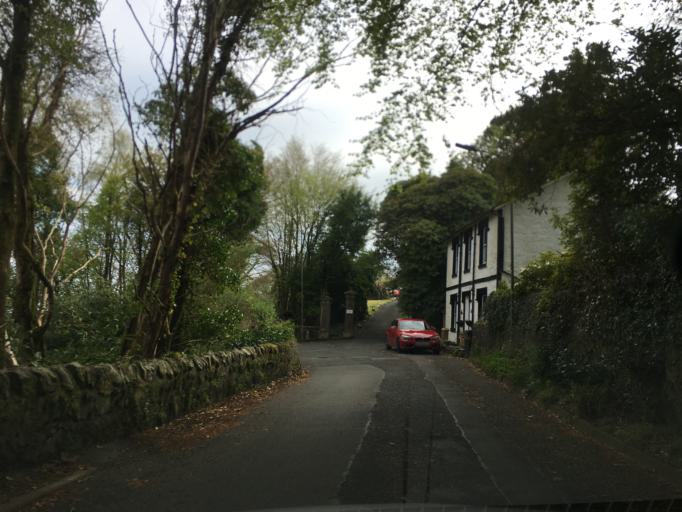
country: GB
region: Scotland
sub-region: Argyll and Bute
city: Rothesay
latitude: 55.8387
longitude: -5.0260
